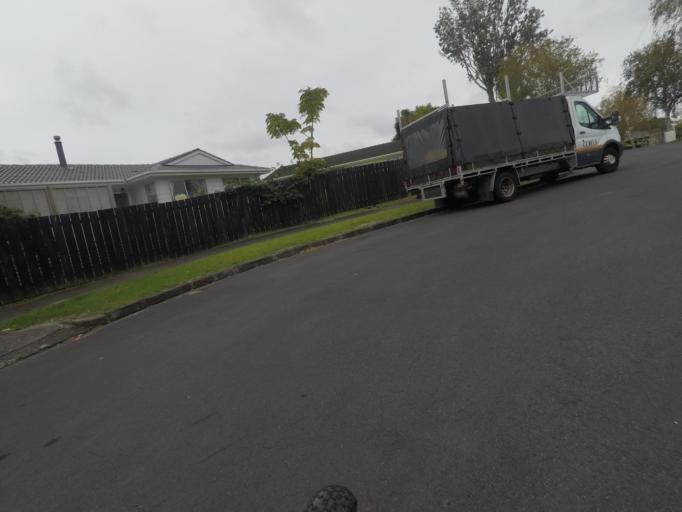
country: NZ
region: Auckland
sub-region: Auckland
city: Rosebank
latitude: -36.8928
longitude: 174.6766
